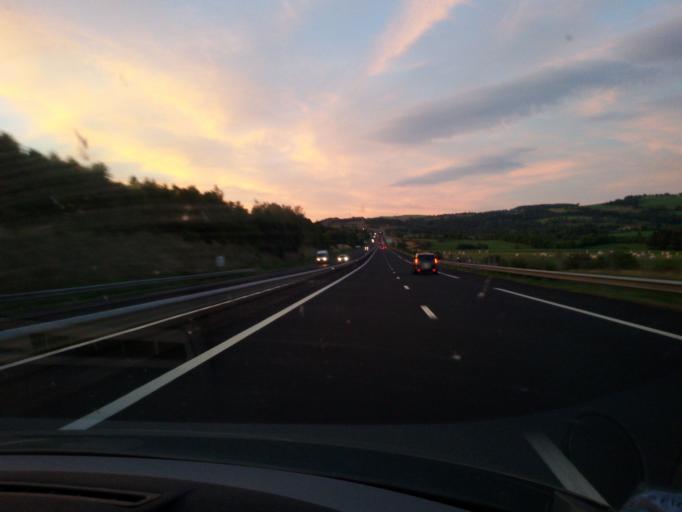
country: FR
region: Auvergne
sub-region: Departement du Cantal
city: Saint-Flour
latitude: 45.0649
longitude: 3.1115
